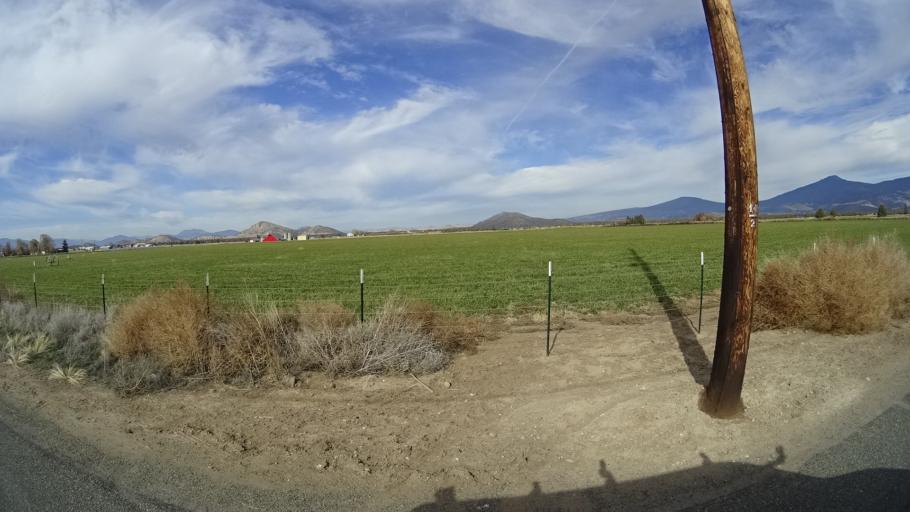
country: US
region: California
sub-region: Siskiyou County
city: Montague
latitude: 41.6165
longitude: -122.3943
